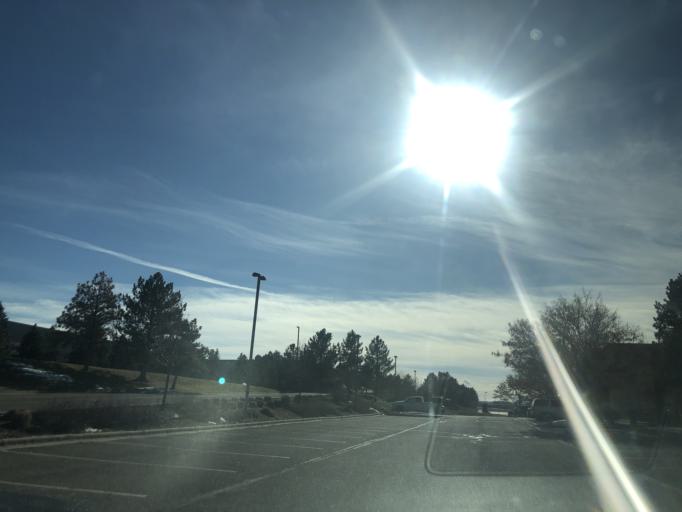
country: US
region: Colorado
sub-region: Douglas County
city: Meridian
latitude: 39.5613
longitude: -104.8594
